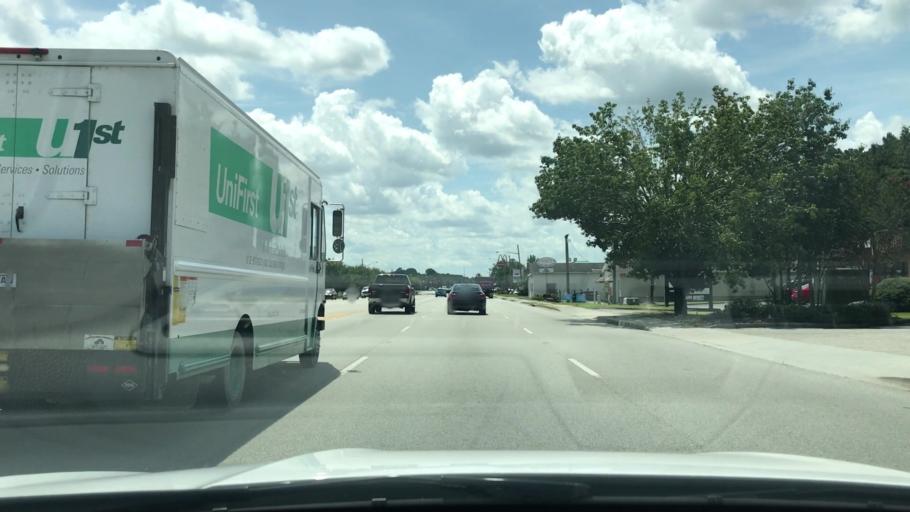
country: US
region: South Carolina
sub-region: Berkeley County
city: Goose Creek
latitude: 33.0010
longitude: -80.0382
